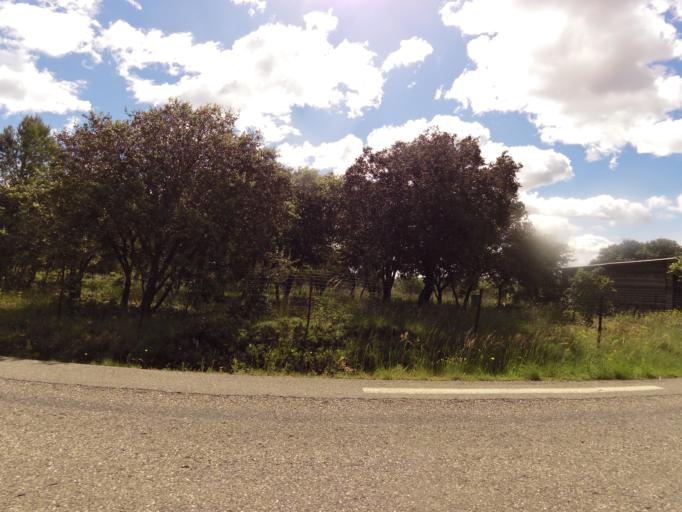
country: FR
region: Languedoc-Roussillon
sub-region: Departement du Gard
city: Mus
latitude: 43.7571
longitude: 4.1995
